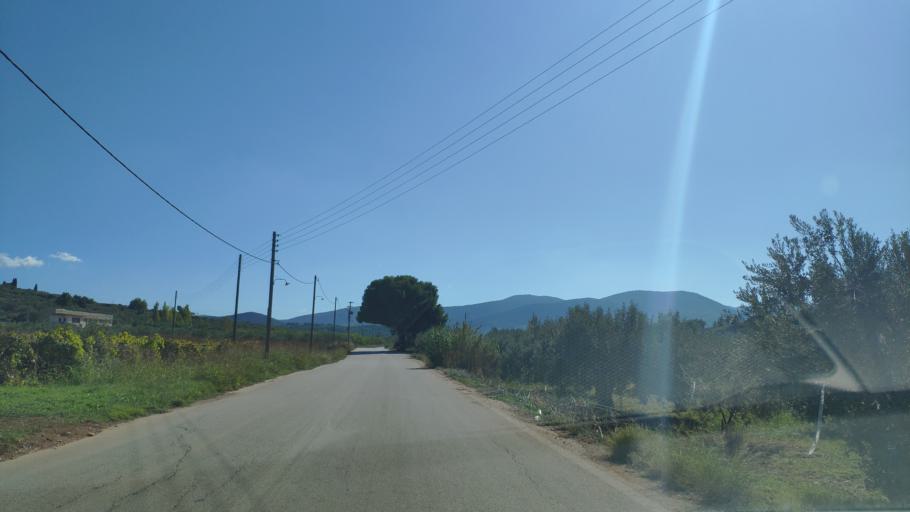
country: GR
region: Peloponnese
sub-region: Nomos Korinthias
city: Athikia
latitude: 37.8464
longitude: 22.9023
